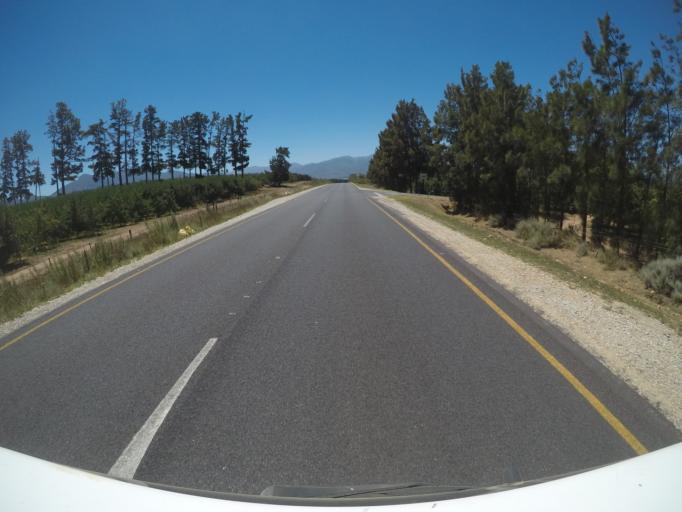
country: ZA
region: Western Cape
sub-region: Overberg District Municipality
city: Grabouw
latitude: -34.0648
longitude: 19.1334
